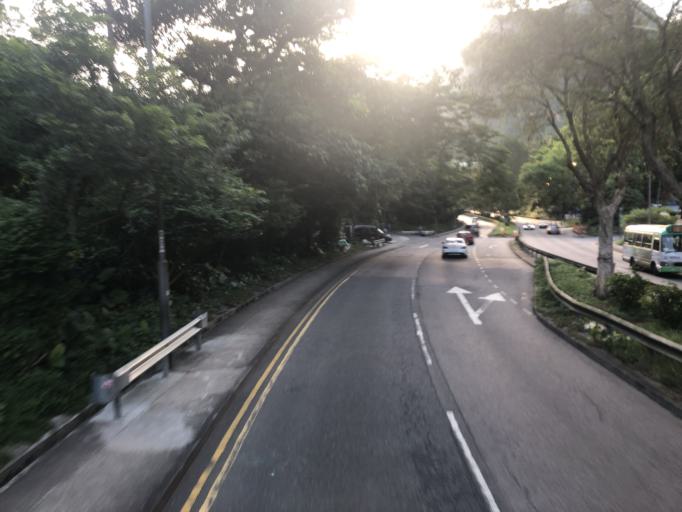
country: HK
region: Kowloon City
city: Kowloon
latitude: 22.3332
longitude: 114.2340
